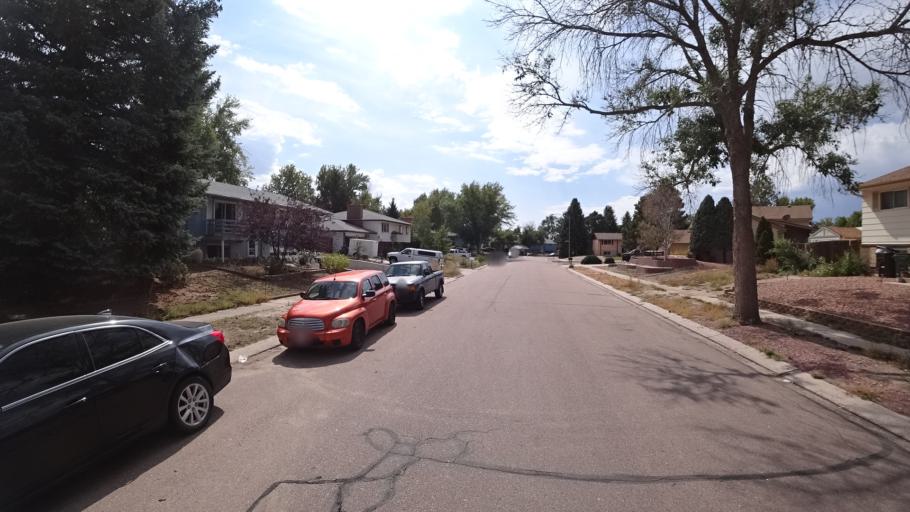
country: US
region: Colorado
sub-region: El Paso County
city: Cimarron Hills
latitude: 38.8507
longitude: -104.7421
